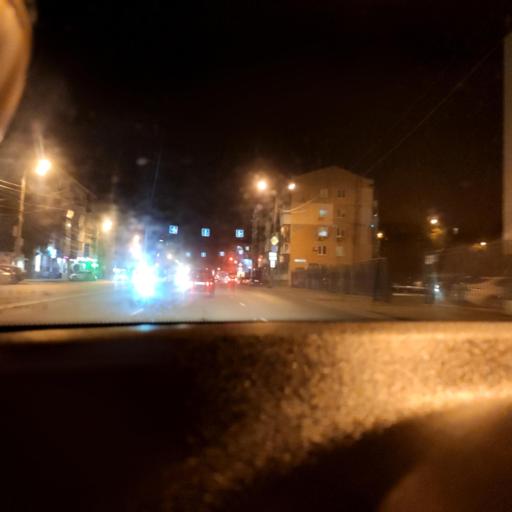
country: RU
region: Samara
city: Samara
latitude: 53.1991
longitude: 50.1904
